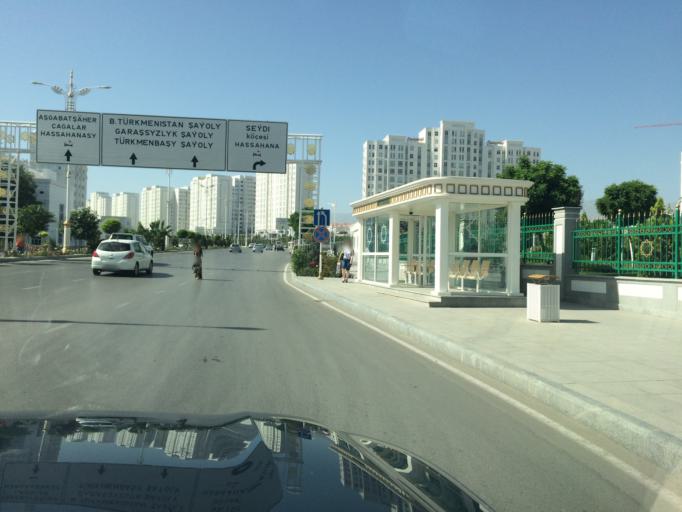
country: TM
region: Ahal
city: Ashgabat
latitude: 37.9416
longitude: 58.3649
